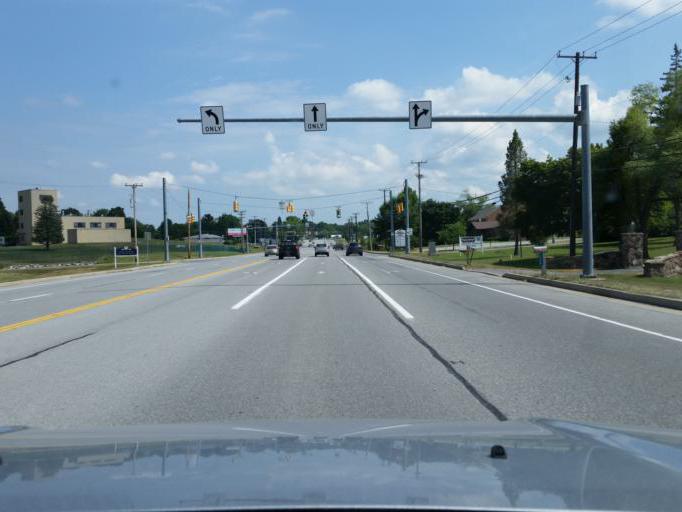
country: US
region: Pennsylvania
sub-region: Blair County
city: Hollidaysburg
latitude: 40.4433
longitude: -78.4118
